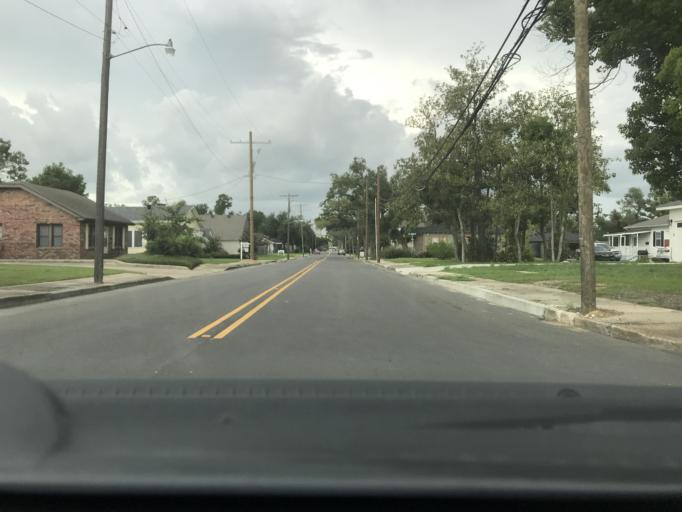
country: US
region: Louisiana
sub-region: Calcasieu Parish
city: Lake Charles
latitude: 30.2141
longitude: -93.2160
